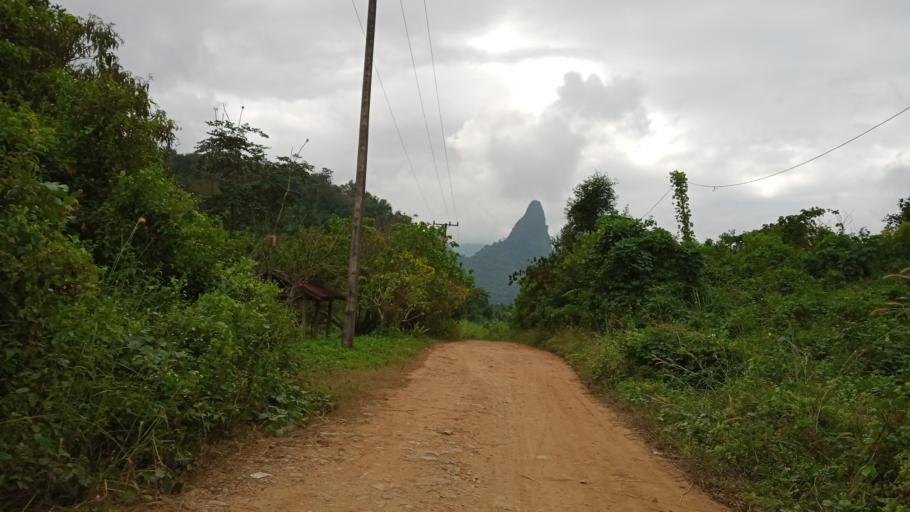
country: LA
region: Xiangkhoang
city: Phonsavan
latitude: 19.0867
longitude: 103.0083
